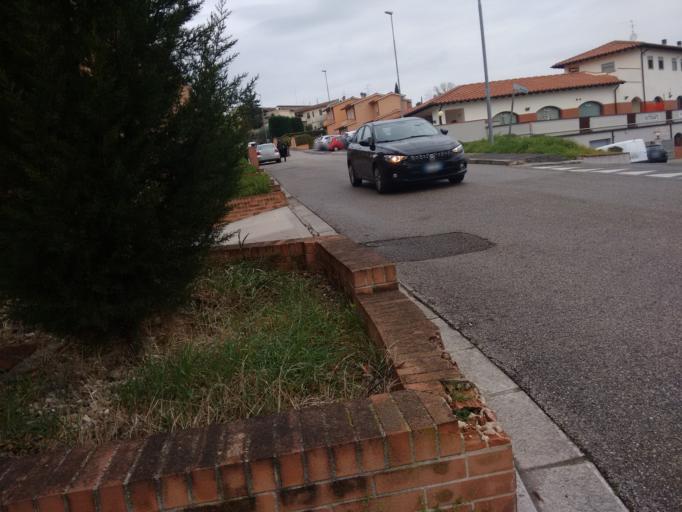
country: IT
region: Tuscany
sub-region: Province of Florence
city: Strada in Chianti
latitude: 43.6577
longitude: 11.3002
